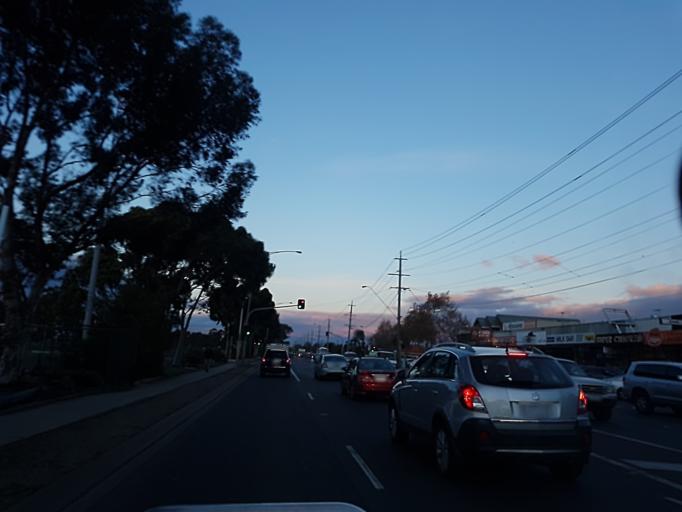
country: AU
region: Victoria
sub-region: Hume
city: Coolaroo
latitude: -37.6665
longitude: 144.9480
